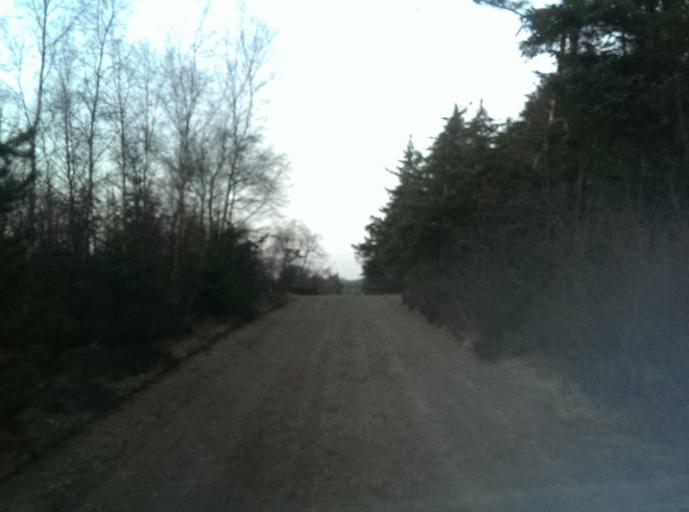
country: DK
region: South Denmark
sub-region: Varde Kommune
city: Oksbol
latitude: 55.5509
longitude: 8.3178
